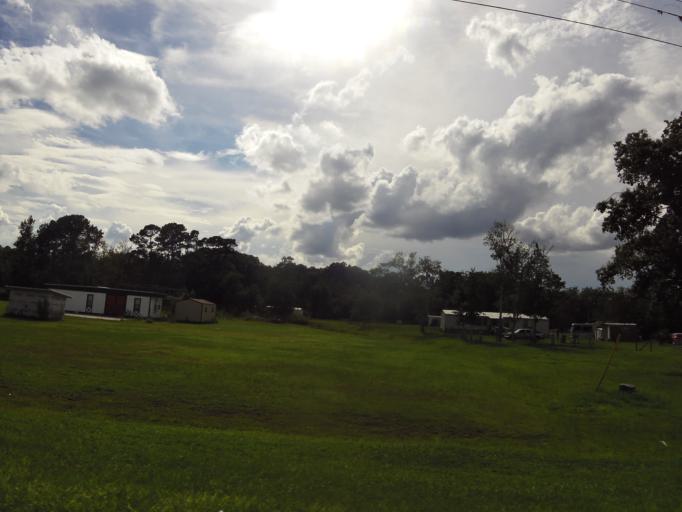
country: US
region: Florida
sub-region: Clay County
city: Green Cove Springs
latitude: 29.9707
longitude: -81.6932
